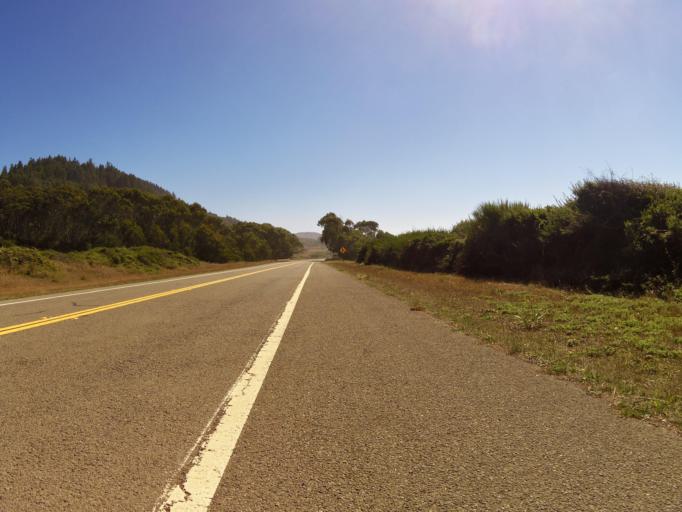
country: US
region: California
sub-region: Mendocino County
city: Fort Bragg
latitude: 39.6800
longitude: -123.7904
